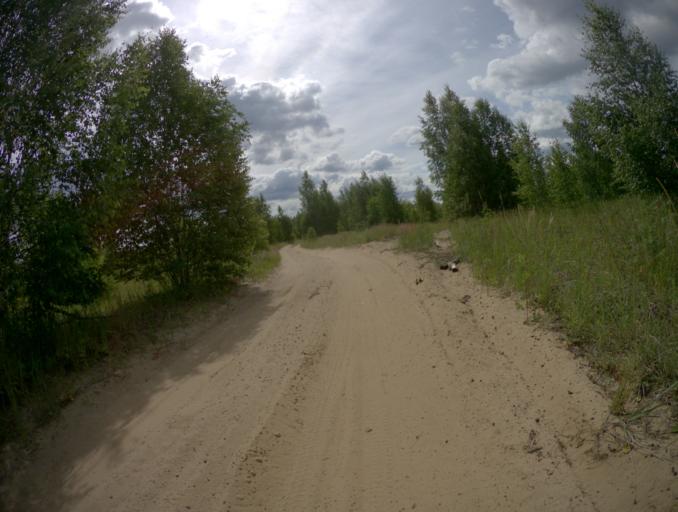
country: RU
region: Ivanovo
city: Talitsy
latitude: 56.5293
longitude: 42.4685
